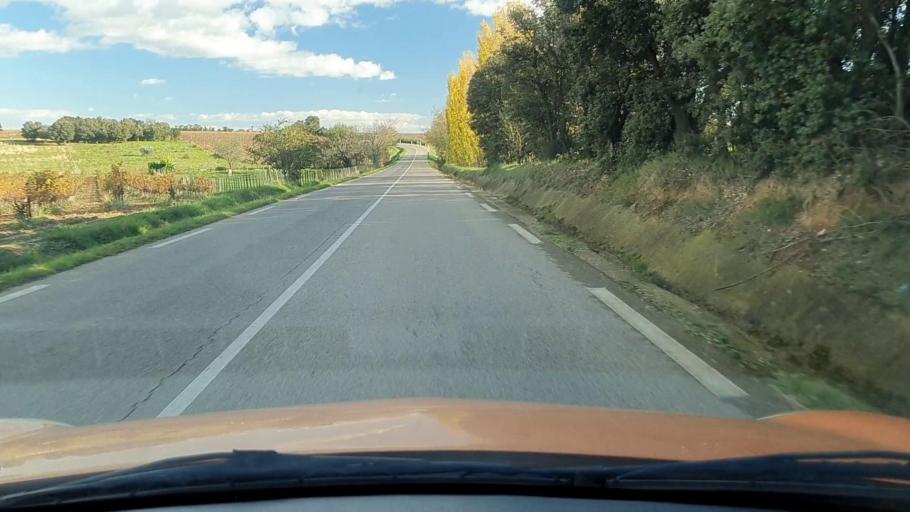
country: FR
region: Languedoc-Roussillon
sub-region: Departement du Gard
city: Vauvert
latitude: 43.6571
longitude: 4.2856
